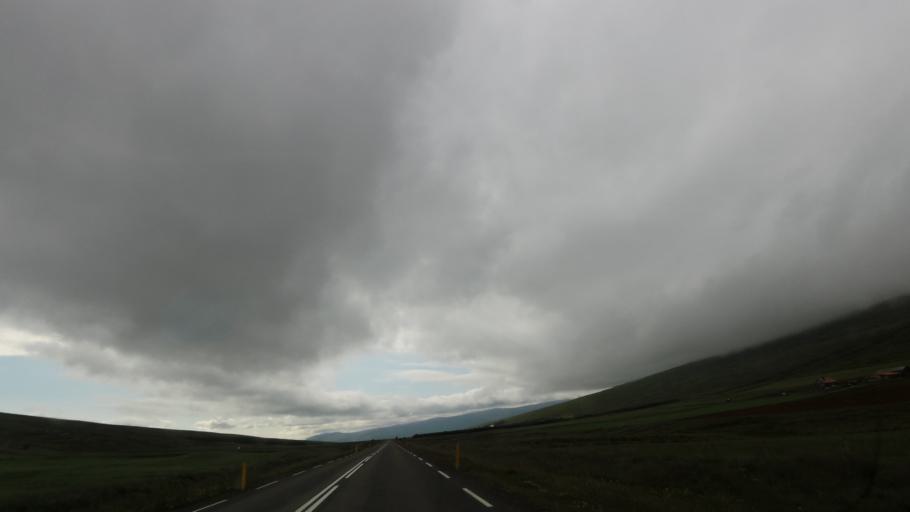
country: IS
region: Northeast
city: Laugar
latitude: 65.7645
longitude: -17.5821
